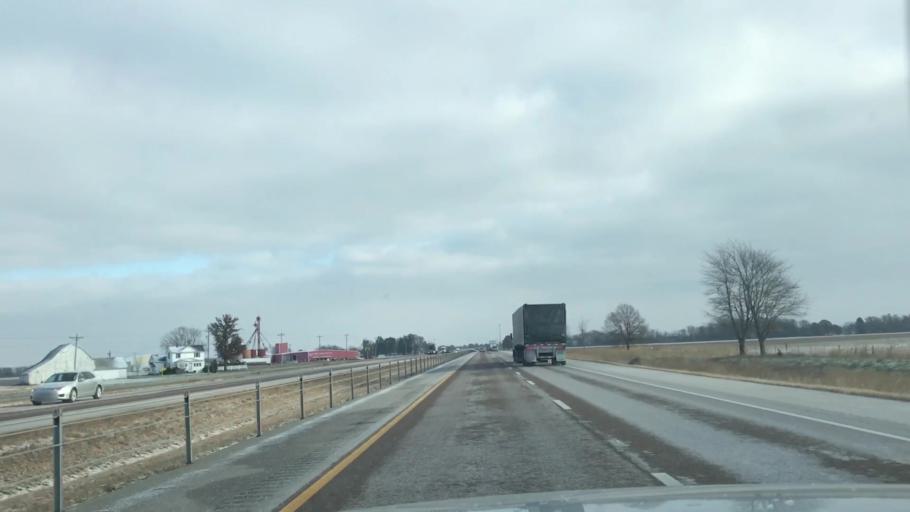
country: US
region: Illinois
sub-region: Madison County
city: Worden
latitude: 38.9208
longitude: -89.8119
